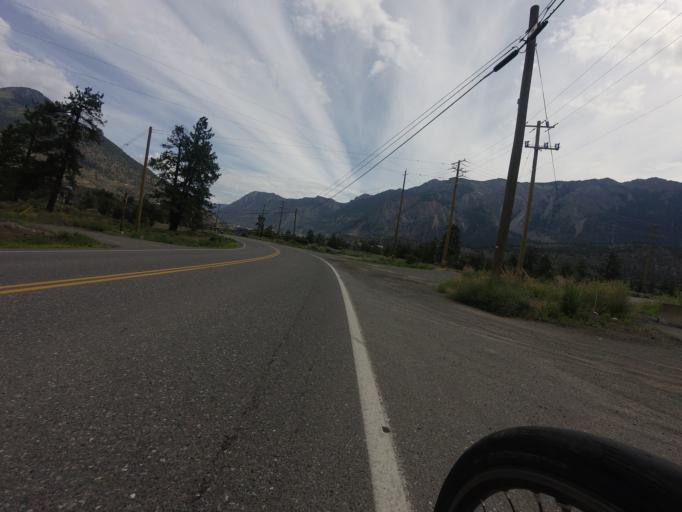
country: CA
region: British Columbia
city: Lillooet
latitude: 50.6771
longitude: -121.9317
